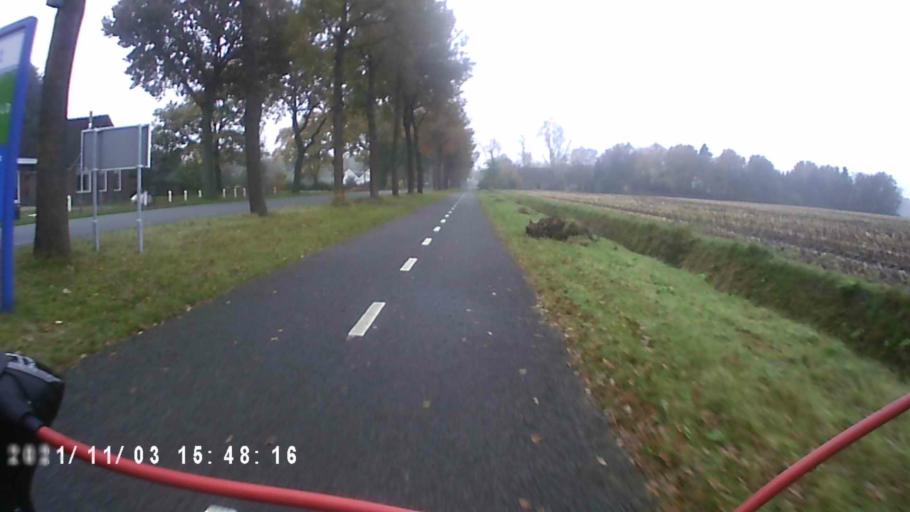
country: NL
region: Groningen
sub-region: Gemeente Leek
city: Leek
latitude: 53.0880
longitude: 6.3392
